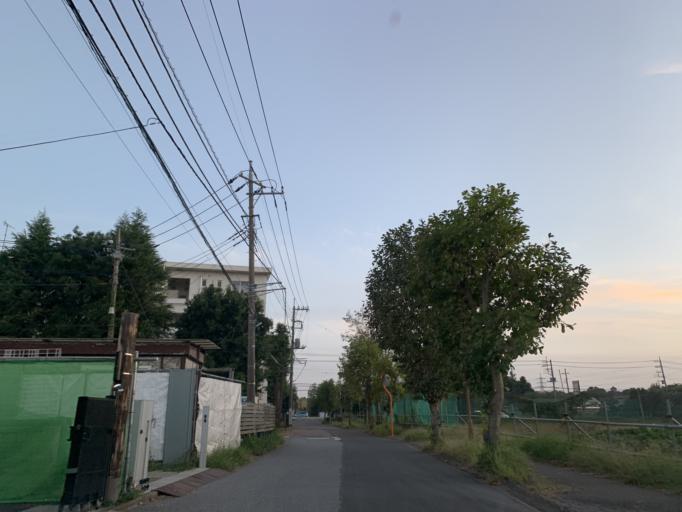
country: JP
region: Chiba
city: Nagareyama
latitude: 35.8882
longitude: 139.9362
